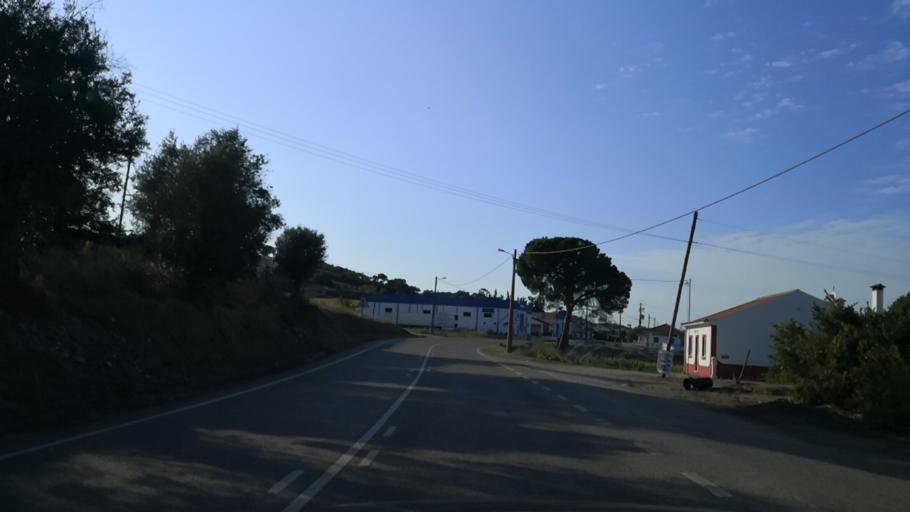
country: PT
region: Santarem
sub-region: Alcanena
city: Alcanena
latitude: 39.3612
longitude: -8.6524
